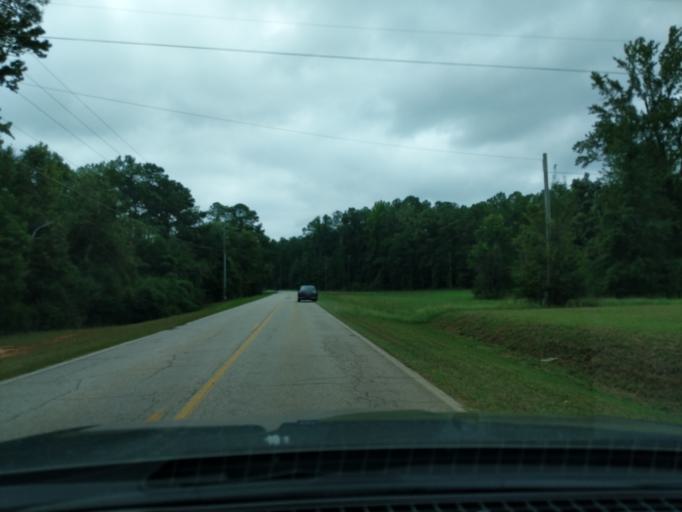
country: US
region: Georgia
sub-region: Columbia County
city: Appling
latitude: 33.6148
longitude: -82.3996
